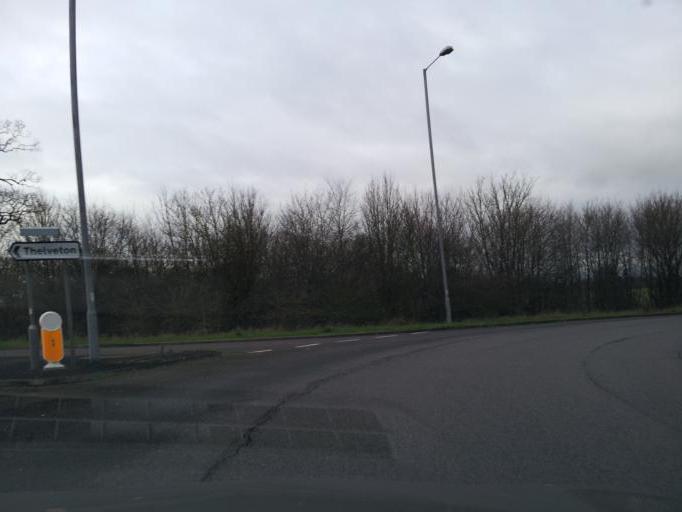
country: GB
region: England
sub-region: Norfolk
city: Diss
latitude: 52.3906
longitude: 1.1798
